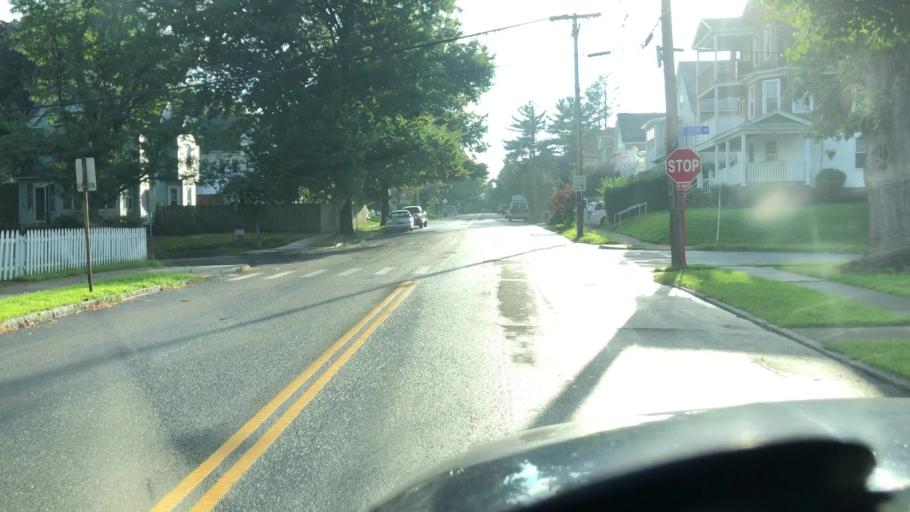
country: US
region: Massachusetts
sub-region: Hampden County
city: Holyoke
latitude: 42.2056
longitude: -72.6252
